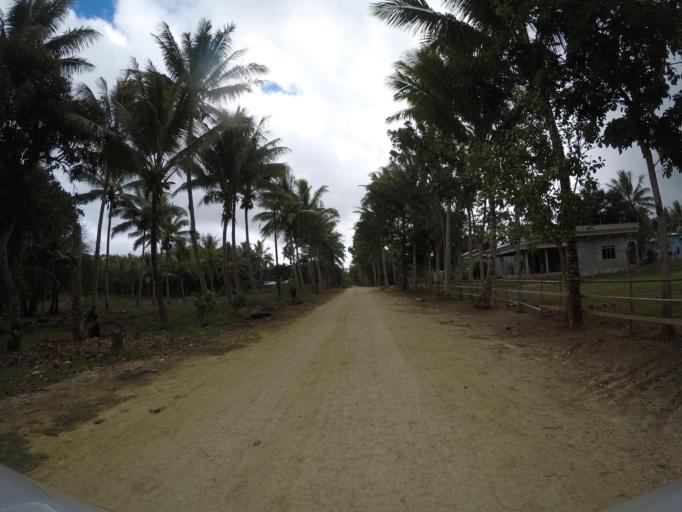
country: TL
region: Lautem
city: Lospalos
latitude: -8.5030
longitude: 126.9958
